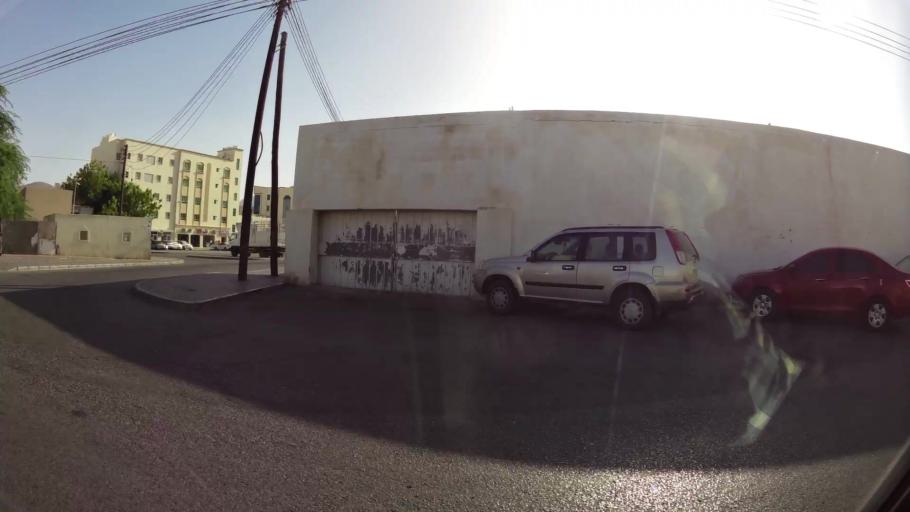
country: OM
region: Muhafazat Masqat
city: Muscat
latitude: 23.5901
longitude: 58.5473
